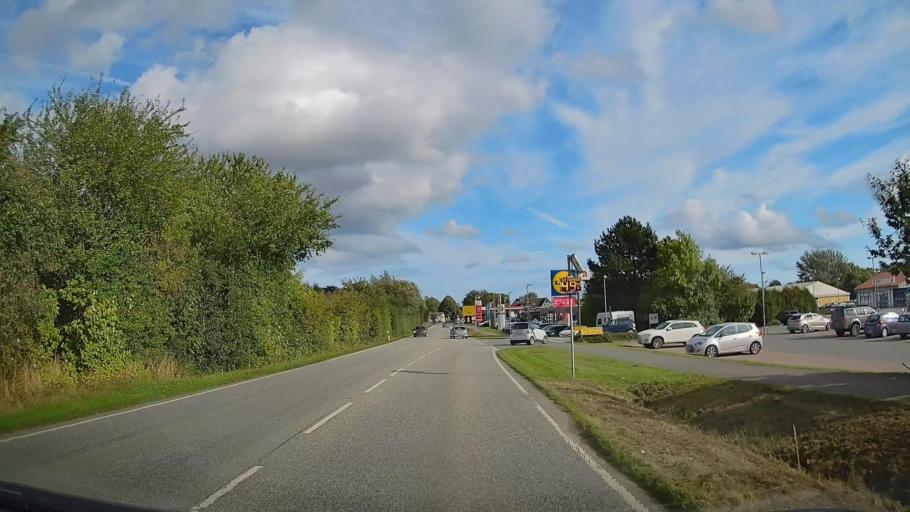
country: DE
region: Schleswig-Holstein
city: Gelting
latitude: 54.7468
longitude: 9.8915
